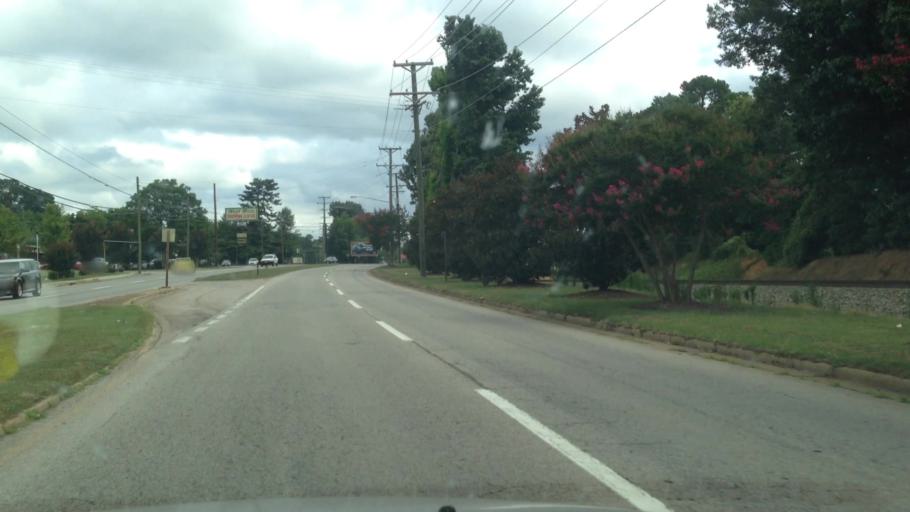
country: US
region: Virginia
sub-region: City of Danville
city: Danville
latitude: 36.5577
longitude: -79.4578
